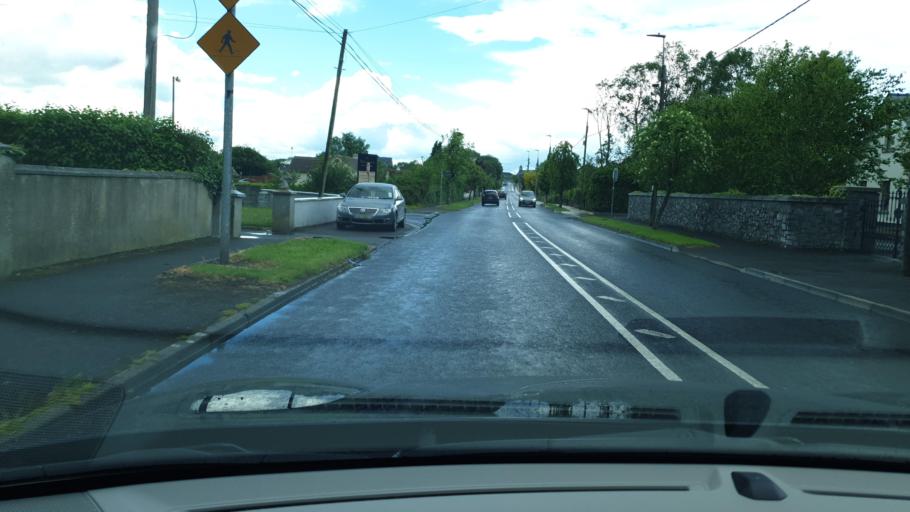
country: IE
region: Connaught
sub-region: County Galway
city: Ballinasloe
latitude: 53.3237
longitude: -8.1936
